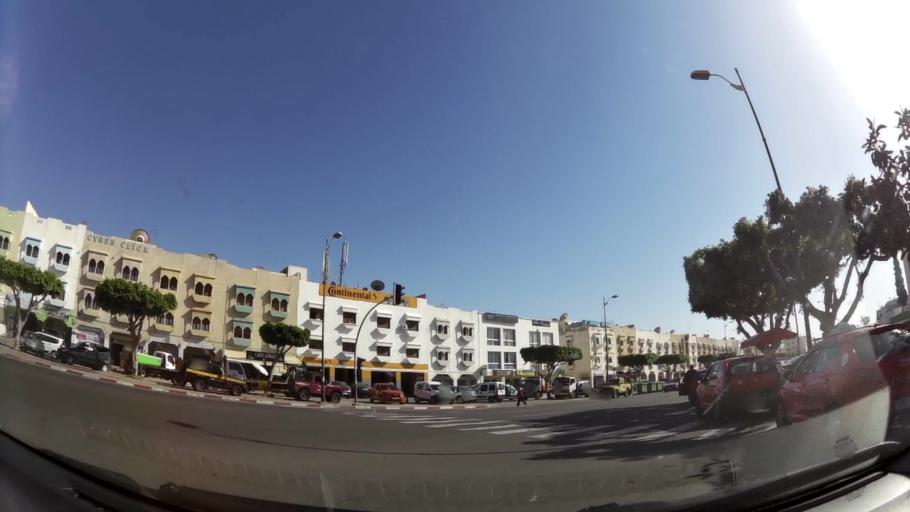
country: MA
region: Oued ed Dahab-Lagouira
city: Dakhla
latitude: 30.4212
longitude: -9.5596
